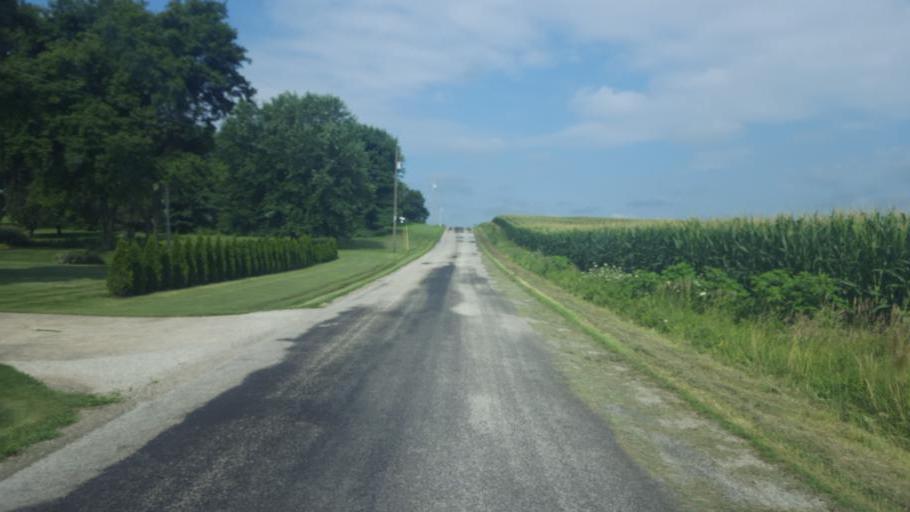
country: US
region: Ohio
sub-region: Crawford County
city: Galion
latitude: 40.6683
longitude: -82.7658
